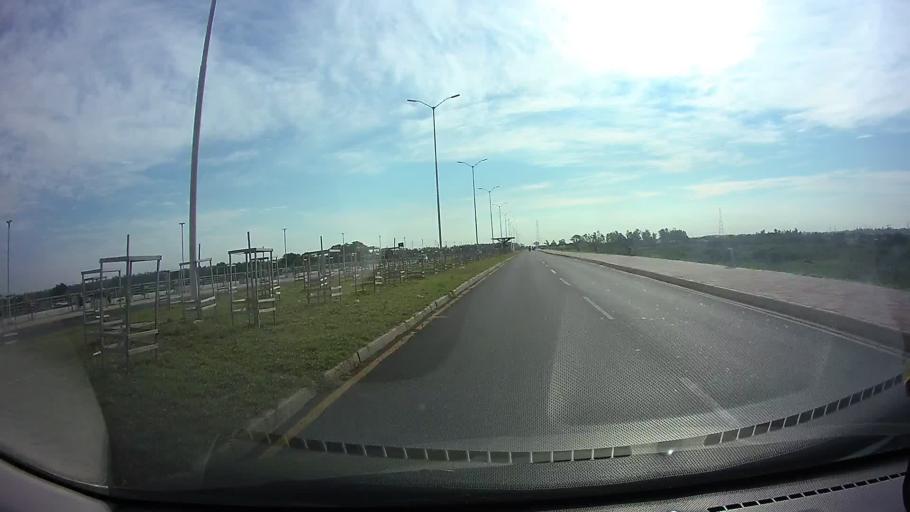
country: PY
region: Asuncion
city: Asuncion
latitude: -25.2558
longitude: -57.6076
